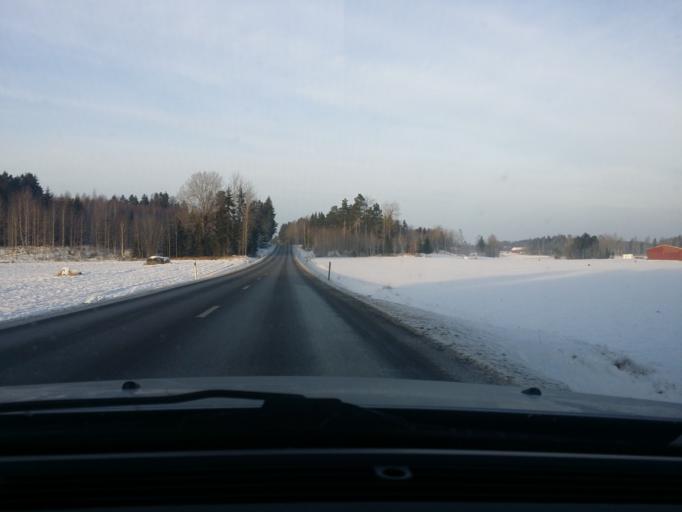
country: SE
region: OErebro
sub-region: Lindesbergs Kommun
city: Frovi
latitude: 59.5126
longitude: 15.3473
